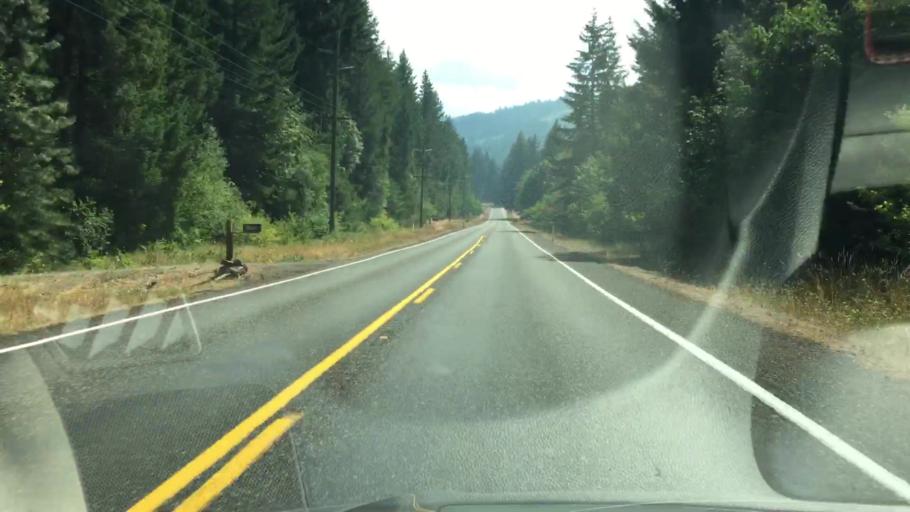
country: US
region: Washington
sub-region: Klickitat County
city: White Salmon
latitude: 45.8586
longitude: -121.5108
